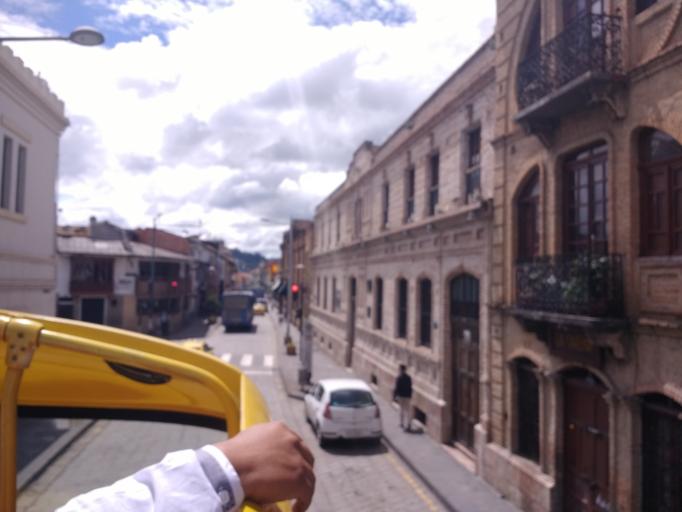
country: EC
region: Azuay
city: Cuenca
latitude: -2.9017
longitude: -79.0042
